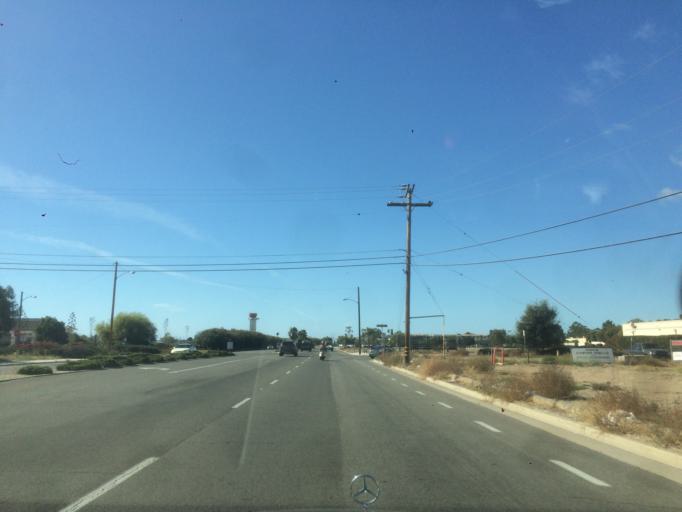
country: US
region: California
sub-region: Santa Barbara County
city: Goleta
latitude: 34.4339
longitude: -119.8376
